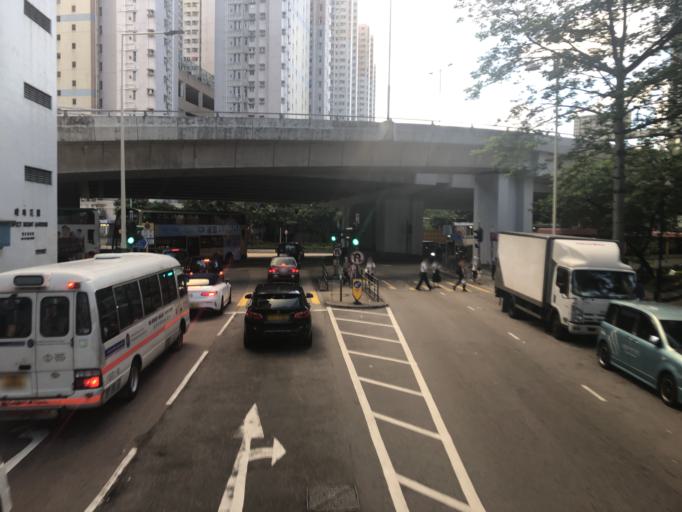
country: HK
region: Wanchai
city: Wan Chai
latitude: 22.2780
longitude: 114.2289
